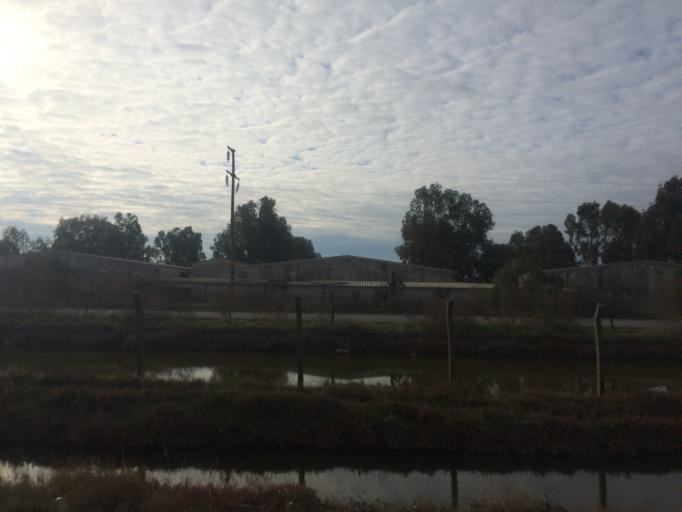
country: TR
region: Izmir
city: Menemen
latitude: 38.4926
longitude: 26.9440
